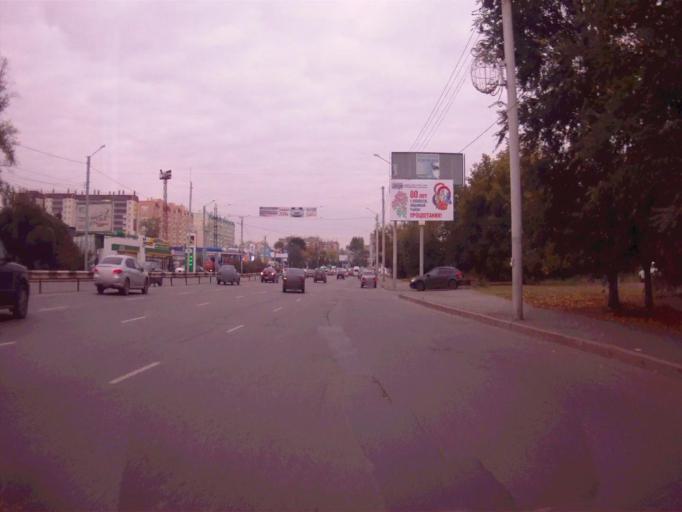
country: RU
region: Chelyabinsk
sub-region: Gorod Chelyabinsk
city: Chelyabinsk
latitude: 55.1377
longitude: 61.4067
